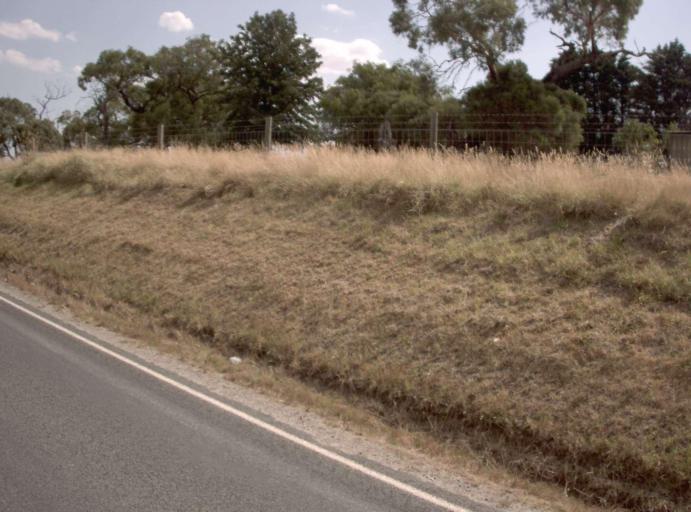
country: AU
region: Victoria
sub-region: Casey
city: Junction Village
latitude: -38.1423
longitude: 145.3225
